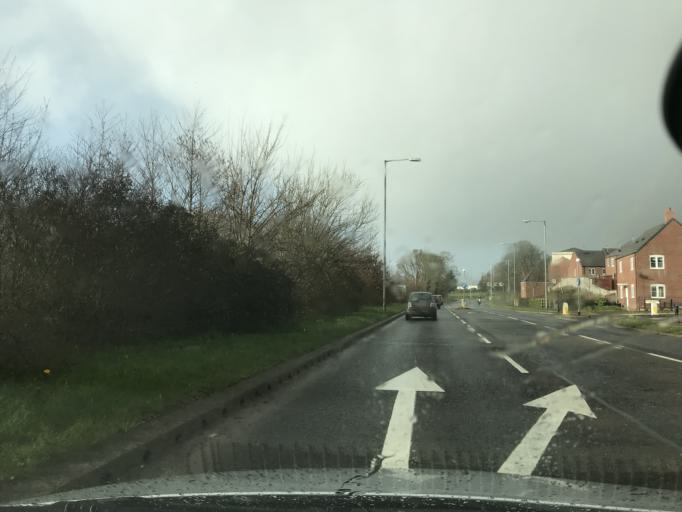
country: GB
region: England
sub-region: Somerset
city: Taunton
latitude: 51.0293
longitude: -3.1332
